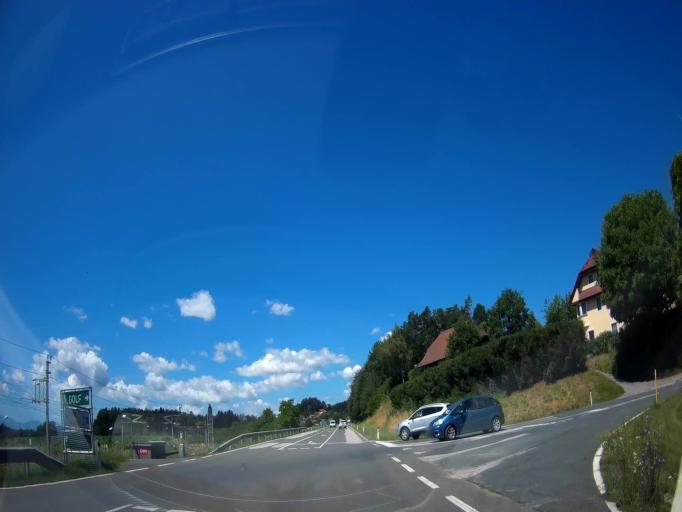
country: AT
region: Carinthia
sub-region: Politischer Bezirk Sankt Veit an der Glan
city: St. Georgen am Laengsee
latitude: 46.7622
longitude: 14.4232
